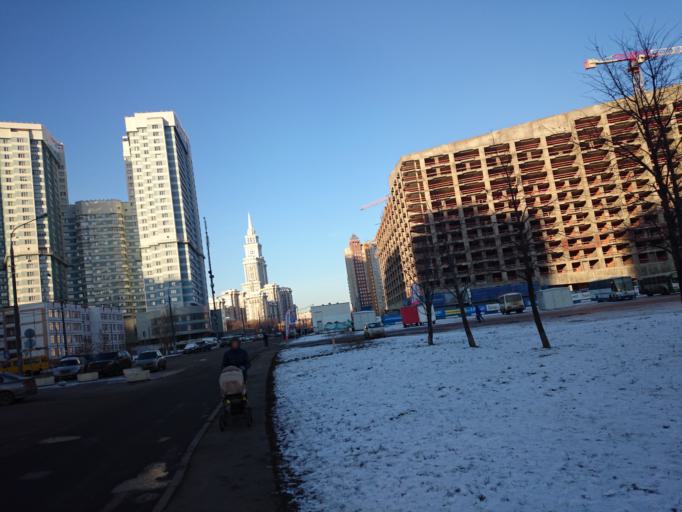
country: RU
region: Moscow
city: Sokol
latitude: 55.7890
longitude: 37.5225
